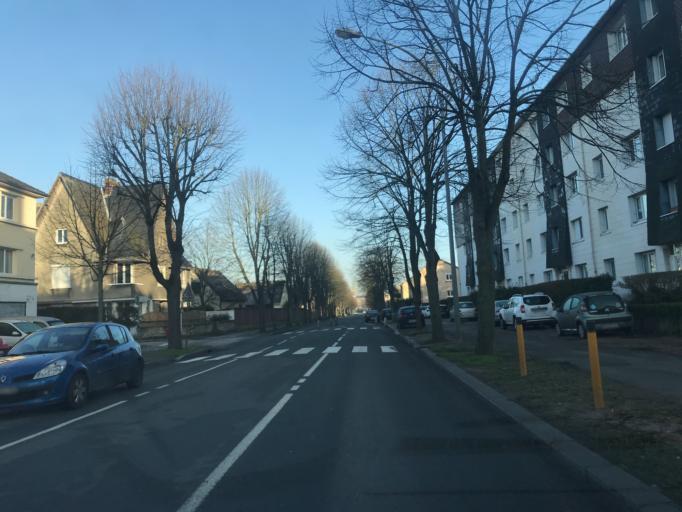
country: FR
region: Haute-Normandie
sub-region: Departement de la Seine-Maritime
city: Sotteville-les-Rouen
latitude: 49.4087
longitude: 1.1011
